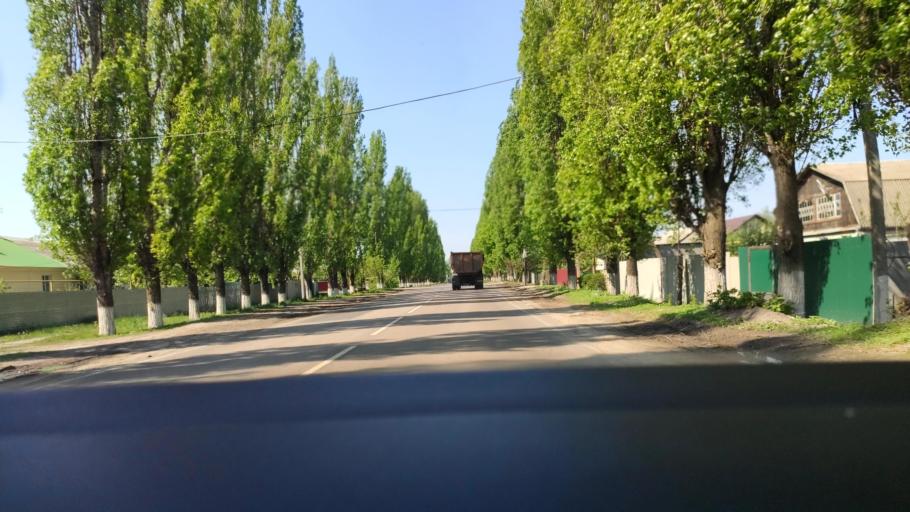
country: RU
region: Voronezj
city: Maslovka
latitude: 51.5371
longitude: 39.3323
